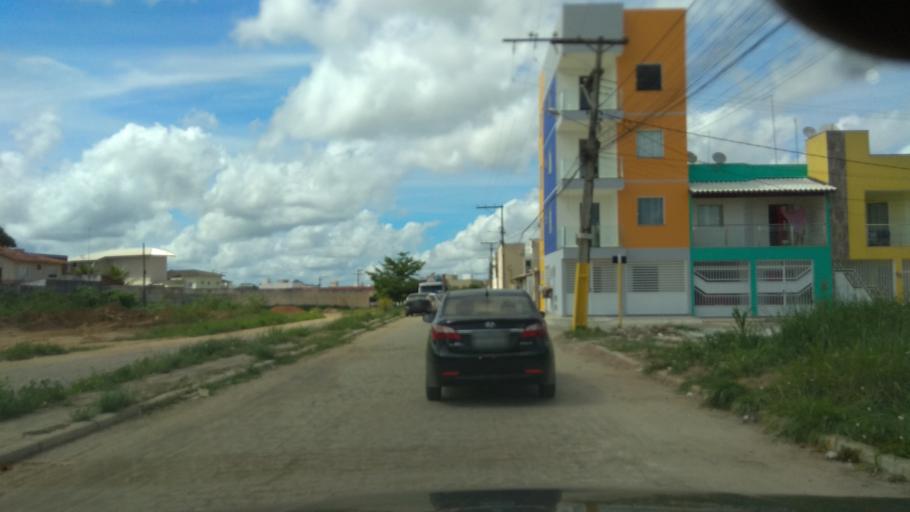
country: BR
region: Bahia
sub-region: Santo Antonio De Jesus
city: Santo Antonio de Jesus
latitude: -12.9799
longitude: -39.2600
